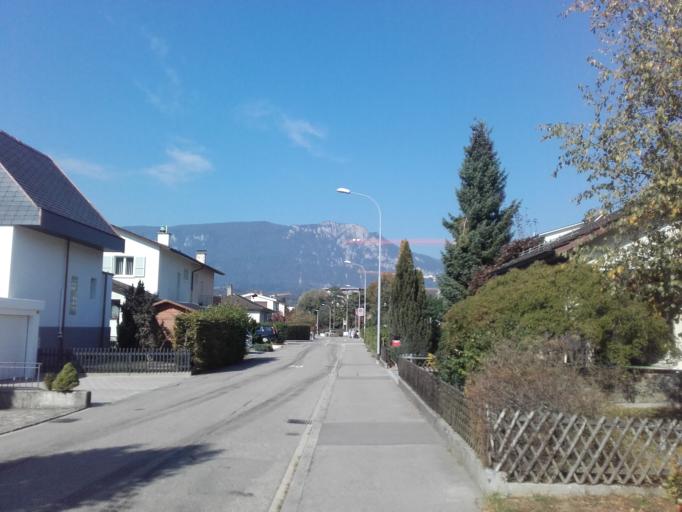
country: CH
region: Solothurn
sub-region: Bezirk Wasseramt
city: Zuchwil
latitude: 47.2109
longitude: 7.5621
